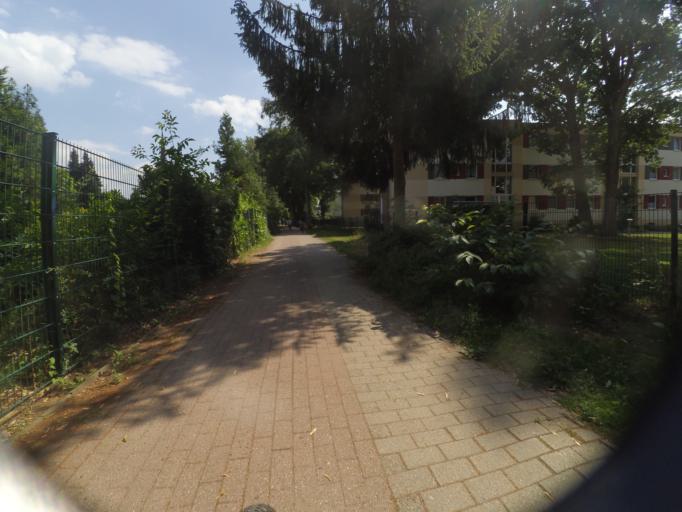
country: DE
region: Hamburg
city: Eidelstedt
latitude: 53.5743
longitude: 9.8678
